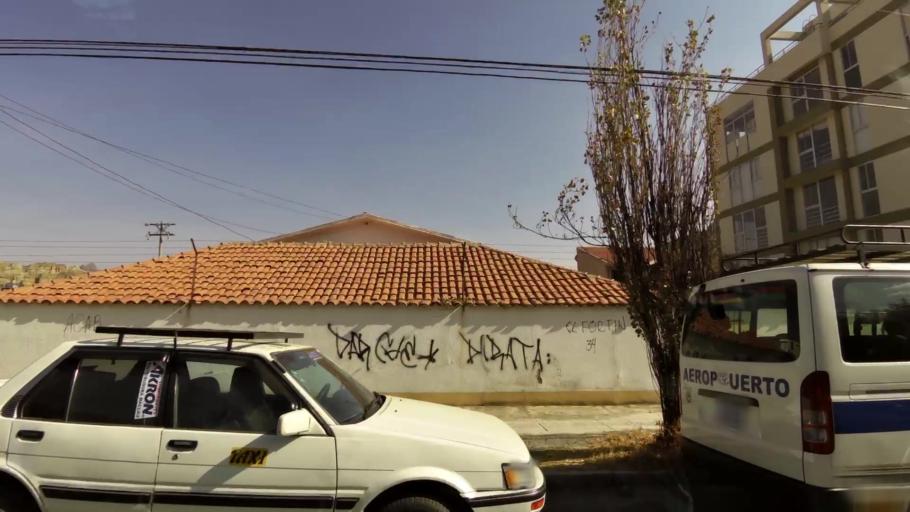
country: BO
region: La Paz
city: La Paz
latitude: -16.5166
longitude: -68.0633
